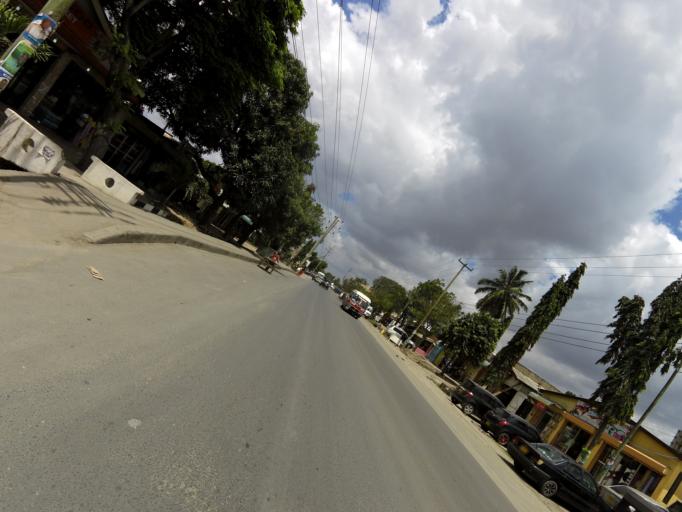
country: TZ
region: Dar es Salaam
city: Magomeni
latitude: -6.7887
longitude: 39.2220
